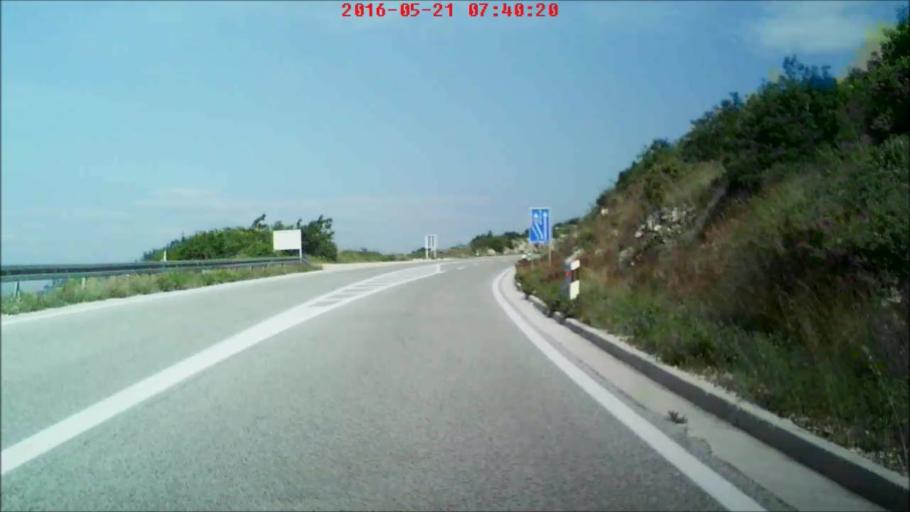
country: HR
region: Dubrovacko-Neretvanska
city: Podgora
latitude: 42.8016
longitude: 17.8288
